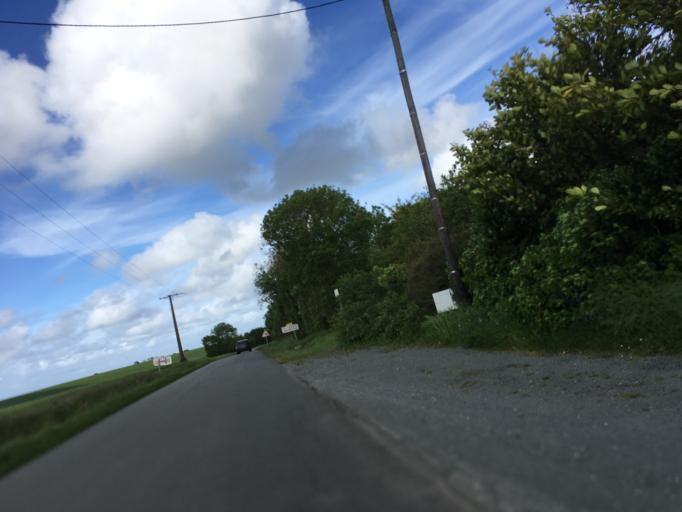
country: FR
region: Poitou-Charentes
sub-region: Departement de la Charente-Maritime
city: Bourgneuf
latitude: 46.1725
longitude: -1.0013
